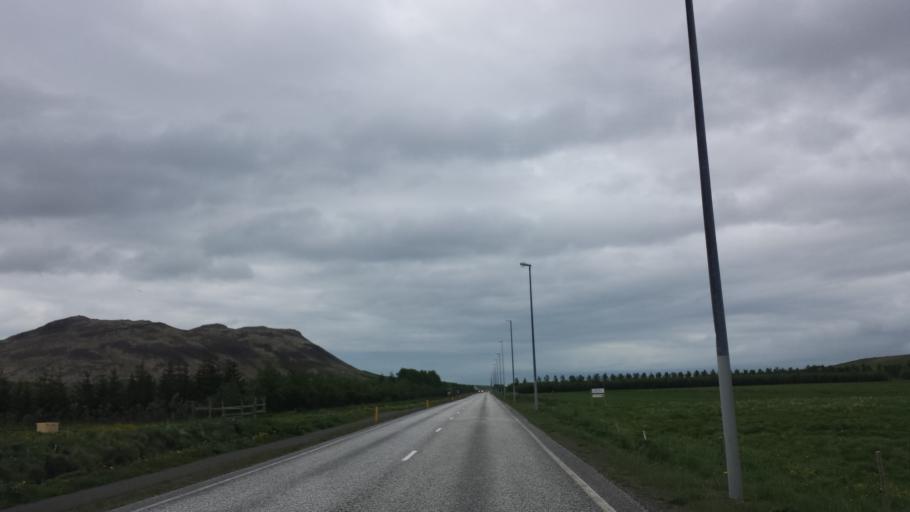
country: IS
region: Capital Region
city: Mosfellsbaer
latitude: 64.1807
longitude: -21.6106
